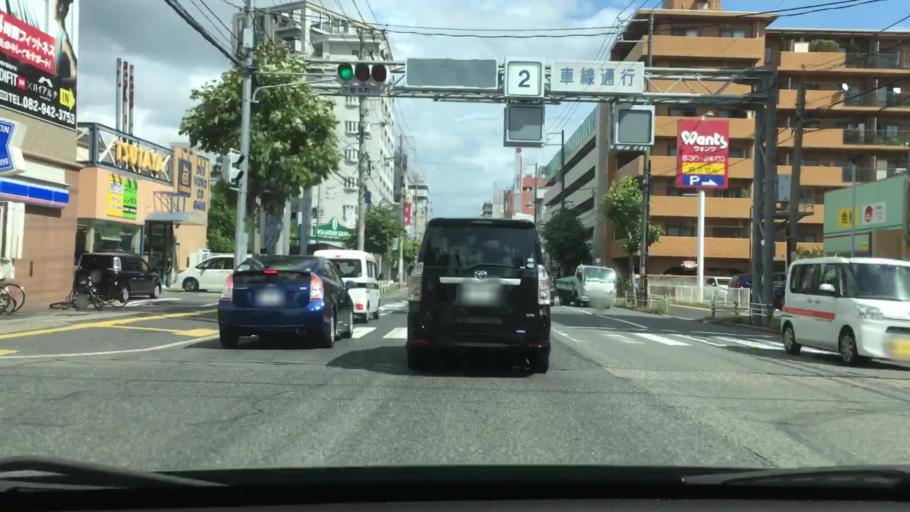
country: JP
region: Hiroshima
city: Hiroshima-shi
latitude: 34.3928
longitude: 132.4245
